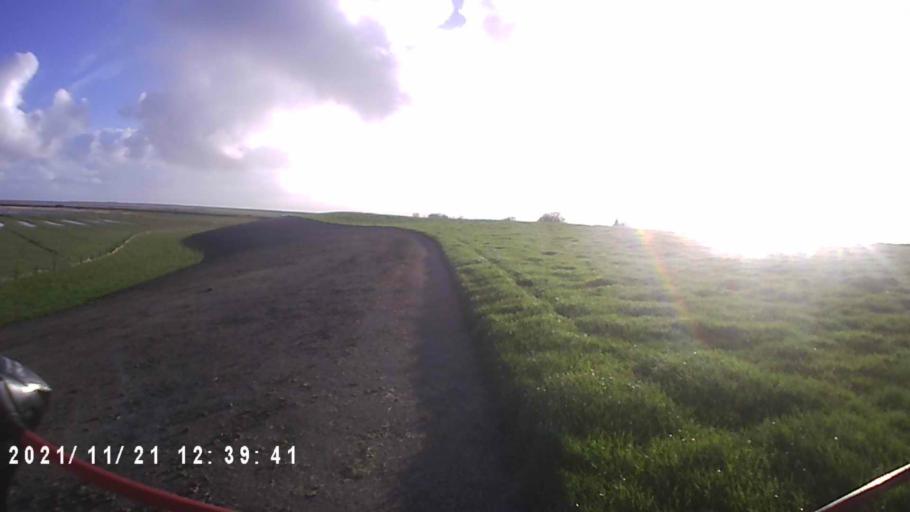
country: NL
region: Friesland
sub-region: Gemeente Dongeradeel
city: Anjum
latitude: 53.4041
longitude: 6.0813
